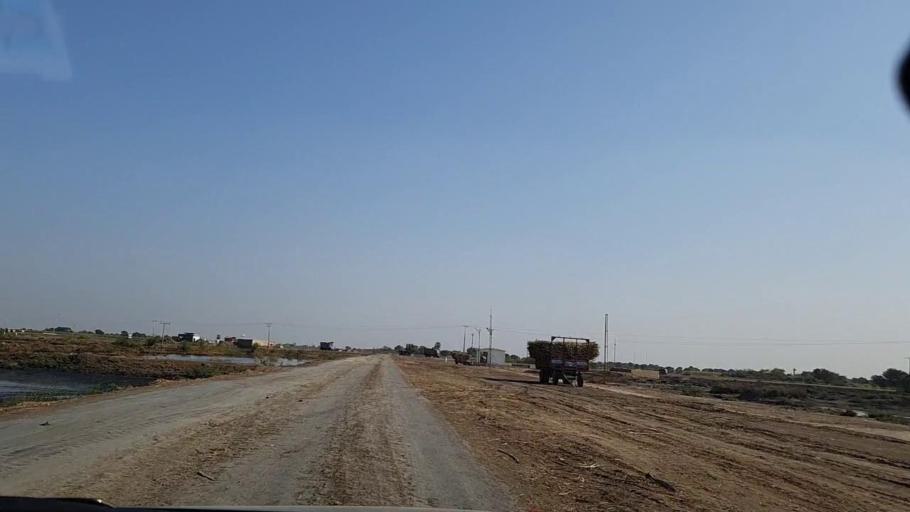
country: PK
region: Sindh
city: Digri
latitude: 25.1592
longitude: 69.0430
